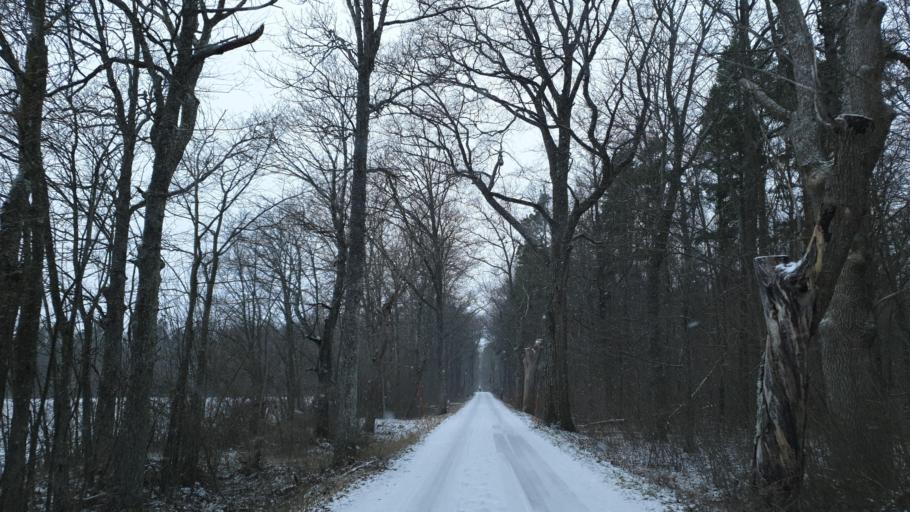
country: SE
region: Gotland
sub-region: Gotland
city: Visby
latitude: 57.5220
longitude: 18.4509
